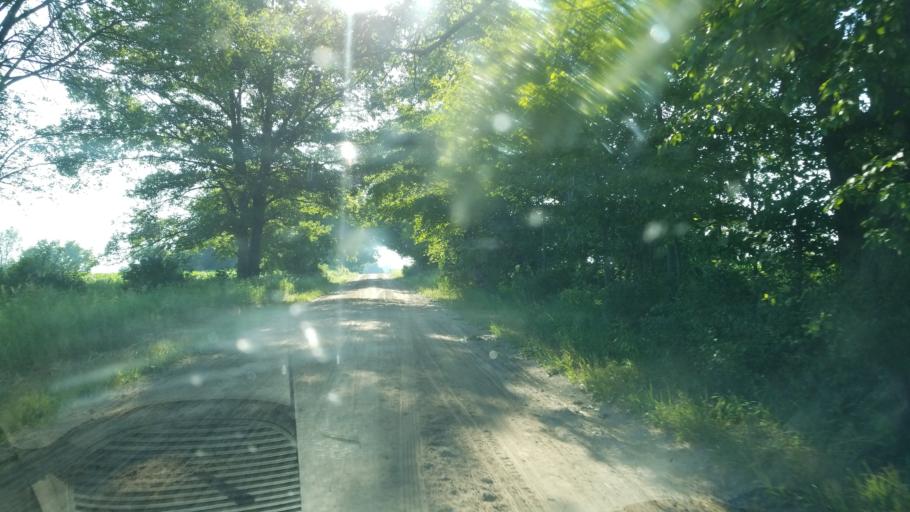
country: US
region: Michigan
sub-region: Mecosta County
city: Canadian Lakes
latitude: 43.5689
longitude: -85.3568
